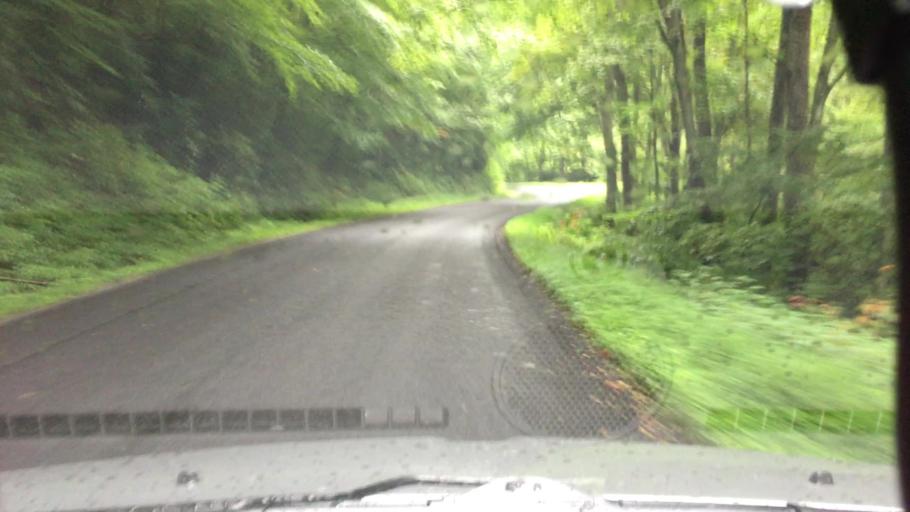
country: US
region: North Carolina
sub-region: Madison County
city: Mars Hill
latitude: 35.9119
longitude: -82.5411
